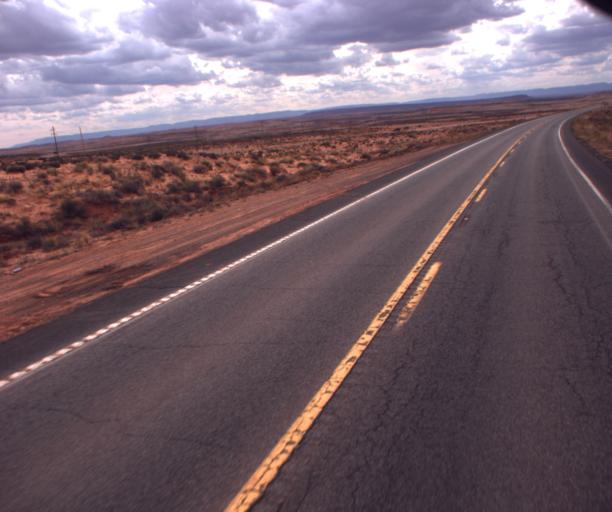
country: US
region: Arizona
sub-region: Navajo County
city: Kayenta
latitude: 36.8965
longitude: -109.7945
